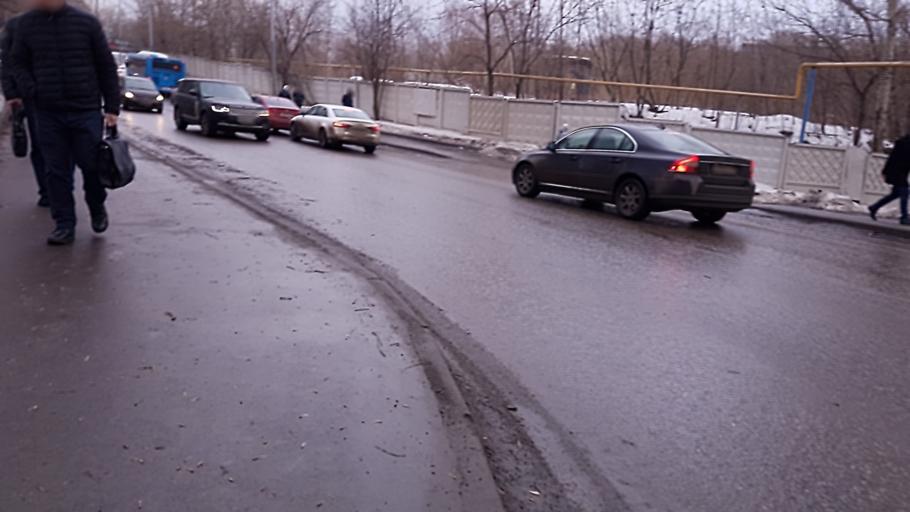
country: RU
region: Moscow
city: Kotlovka
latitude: 55.6884
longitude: 37.6180
